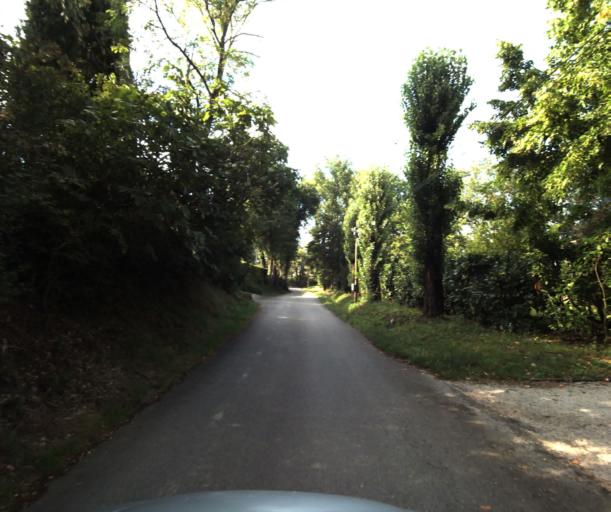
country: FR
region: Midi-Pyrenees
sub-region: Departement de la Haute-Garonne
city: Saubens
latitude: 43.4760
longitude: 1.3487
